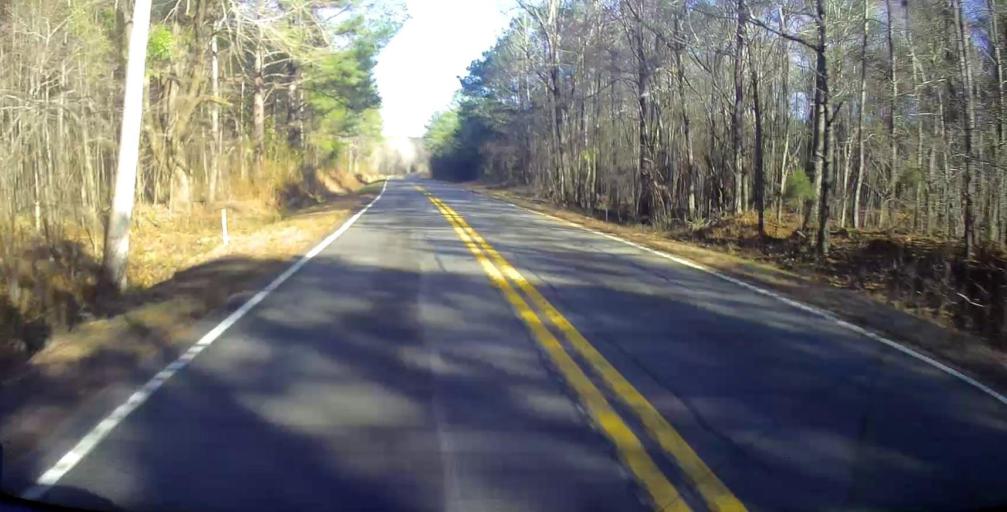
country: US
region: Georgia
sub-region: Talbot County
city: Talbotton
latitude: 32.6726
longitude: -84.5208
